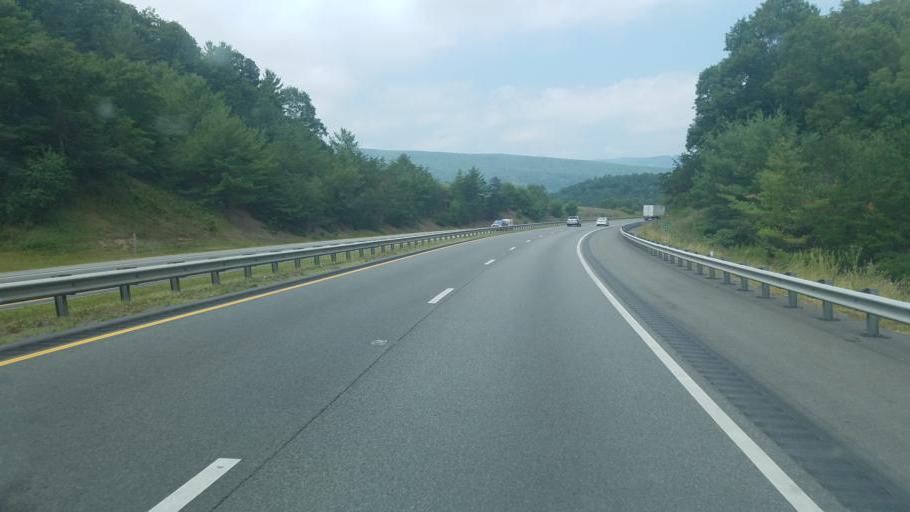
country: US
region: Virginia
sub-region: Bland County
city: Bland
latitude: 37.1412
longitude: -81.1370
